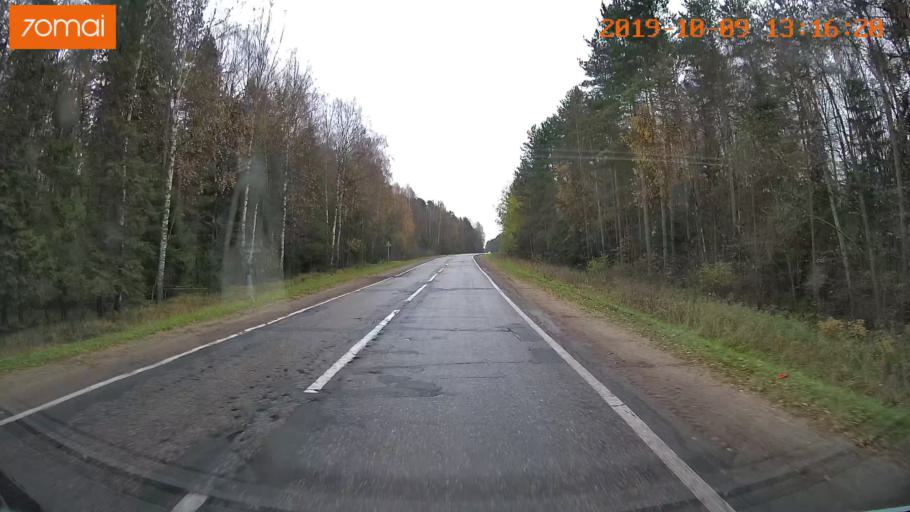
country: RU
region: Jaroslavl
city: Lyubim
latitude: 58.3620
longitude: 40.7643
